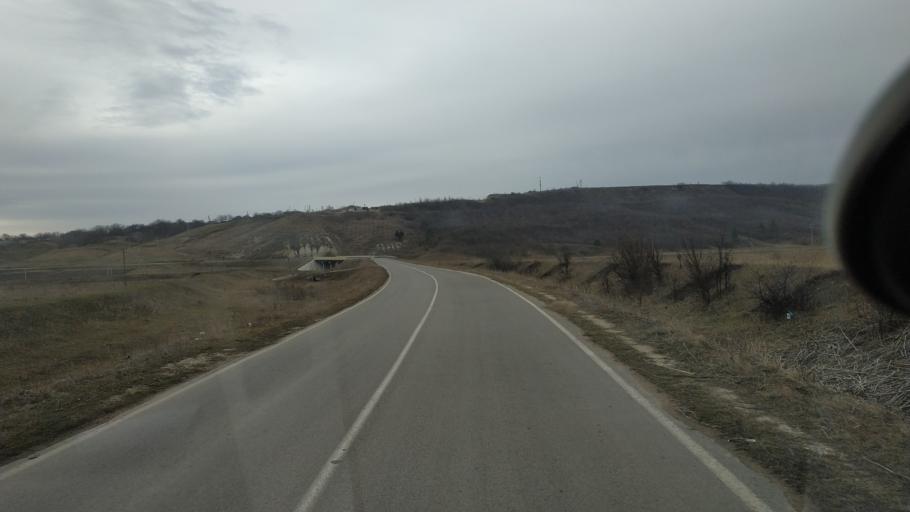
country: MD
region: Telenesti
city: Cocieri
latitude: 47.2650
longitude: 29.0541
